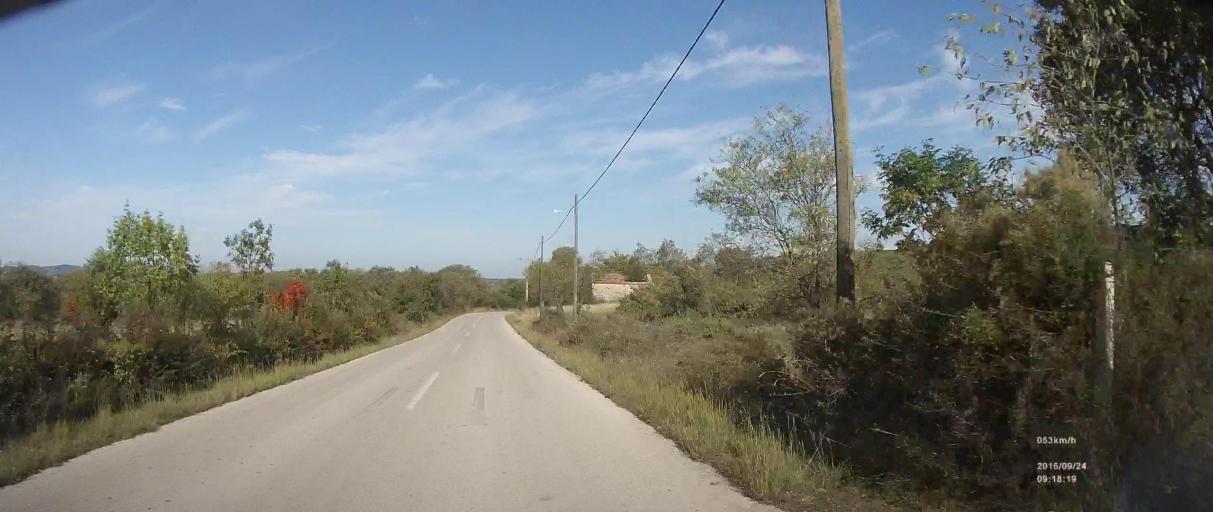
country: HR
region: Zadarska
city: Polaca
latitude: 44.0558
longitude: 15.5130
